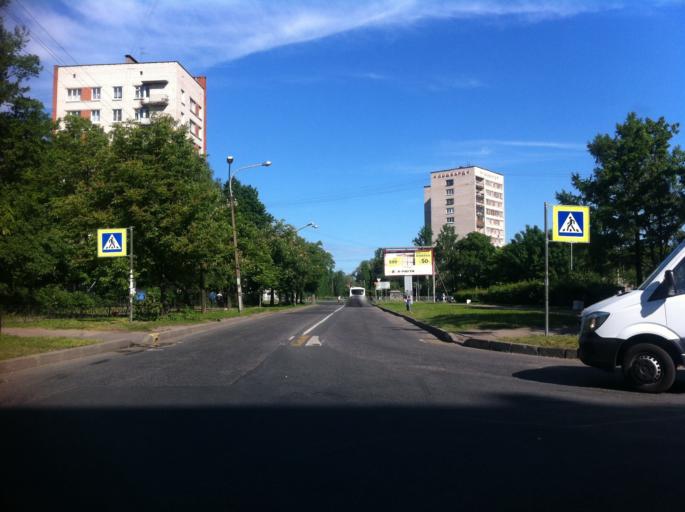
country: RU
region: St.-Petersburg
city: Dachnoye
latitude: 59.8413
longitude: 30.2460
